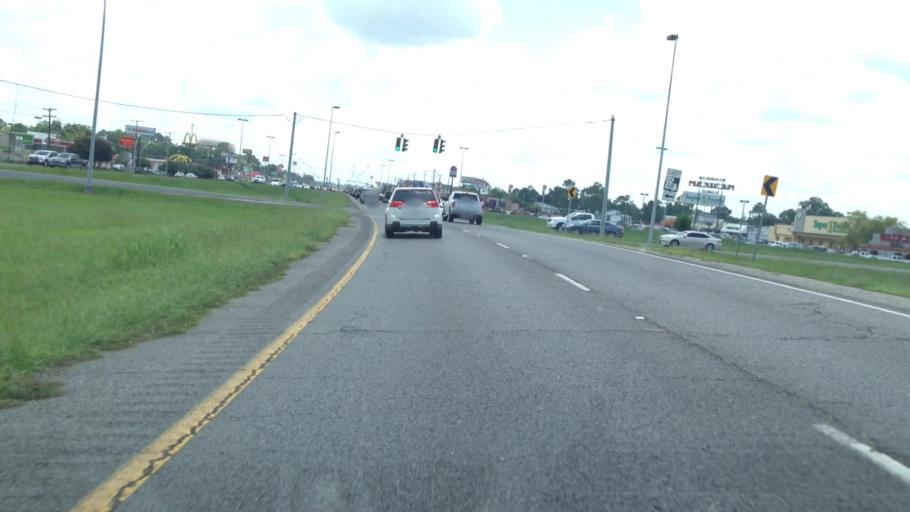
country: US
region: Louisiana
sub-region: Rapides Parish
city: Alexandria
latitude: 31.2995
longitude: -92.4802
